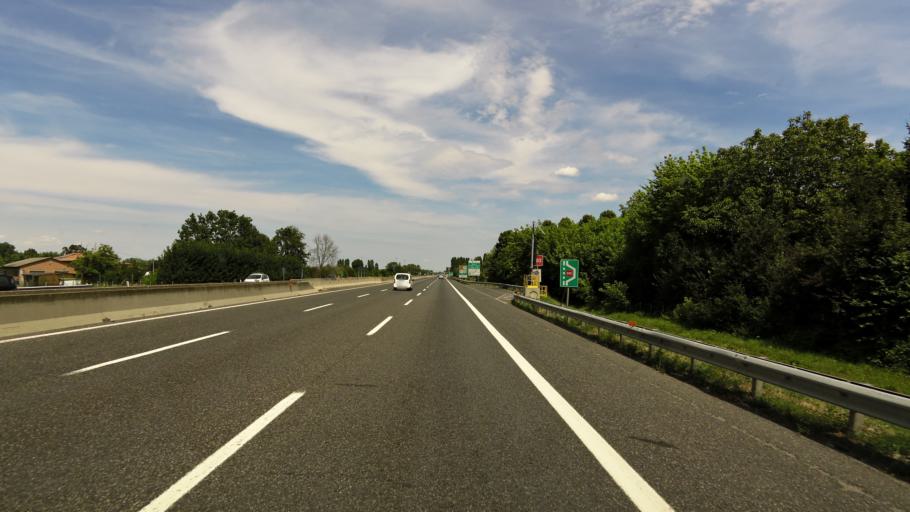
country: IT
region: Emilia-Romagna
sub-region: Provincia di Bologna
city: Ponte Ronca
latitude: 44.5176
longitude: 11.2039
